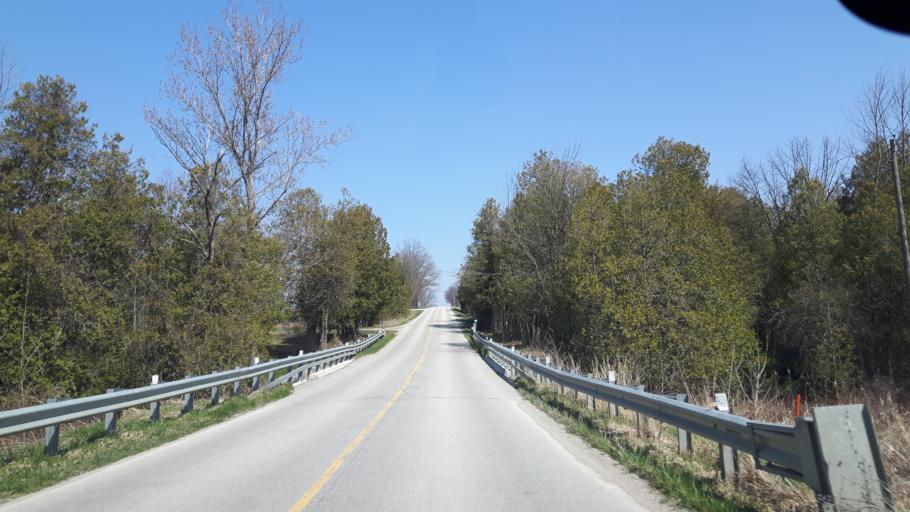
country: CA
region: Ontario
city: Goderich
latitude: 43.6572
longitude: -81.6846
